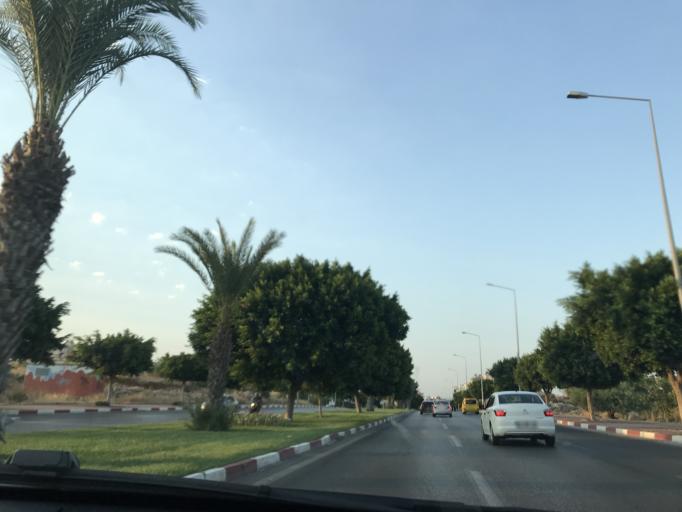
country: TR
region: Antalya
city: Antalya
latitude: 36.8699
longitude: 30.6406
